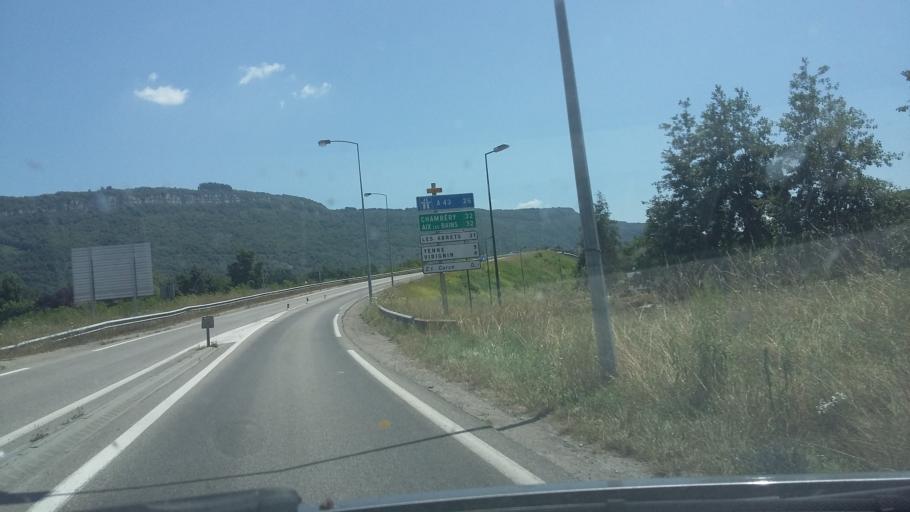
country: FR
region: Rhone-Alpes
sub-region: Departement de l'Ain
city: Belley
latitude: 45.7572
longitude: 5.7061
